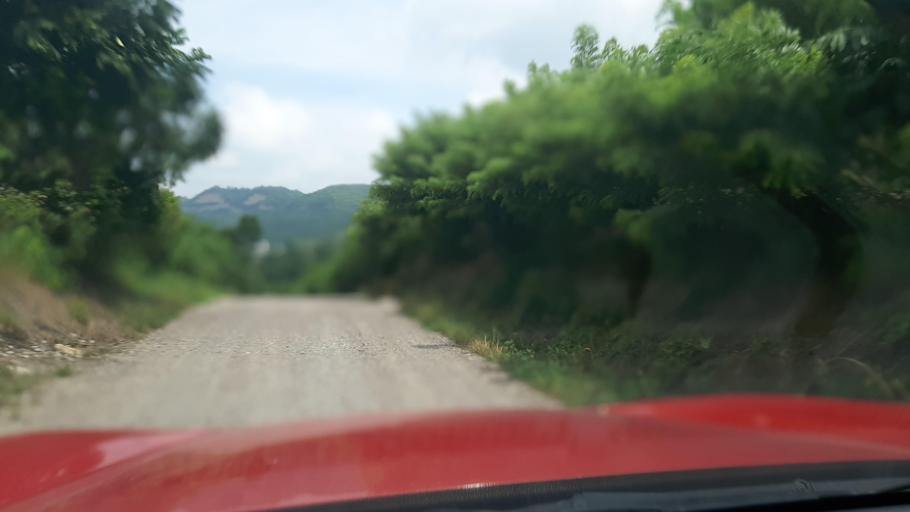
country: MX
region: Veracruz
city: Gutierrez Zamora
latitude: 20.4599
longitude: -97.1828
